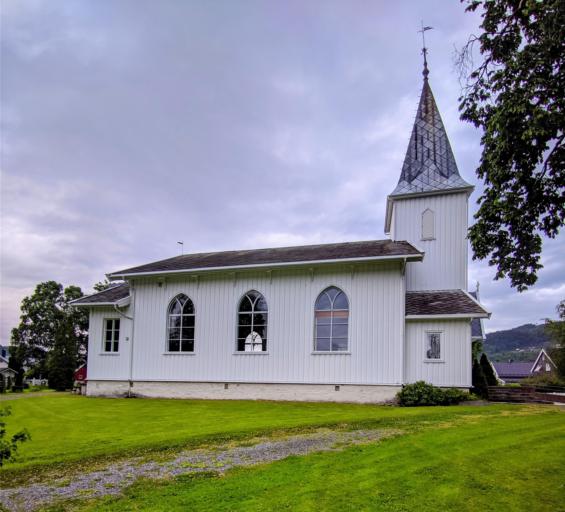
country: NO
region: Sor-Trondelag
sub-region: Orkdal
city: Orkanger
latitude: 63.3099
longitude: 9.8512
